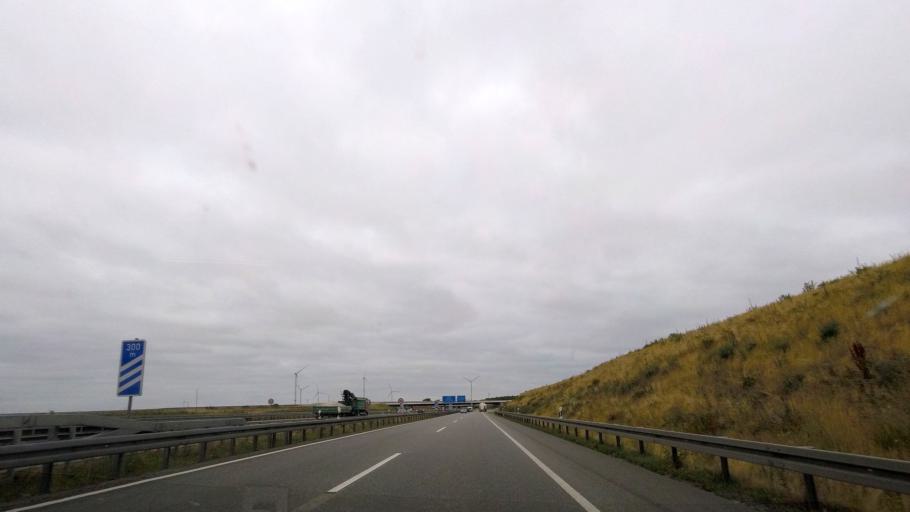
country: DE
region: Brandenburg
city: Ahrensfelde
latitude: 52.6132
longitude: 13.5692
